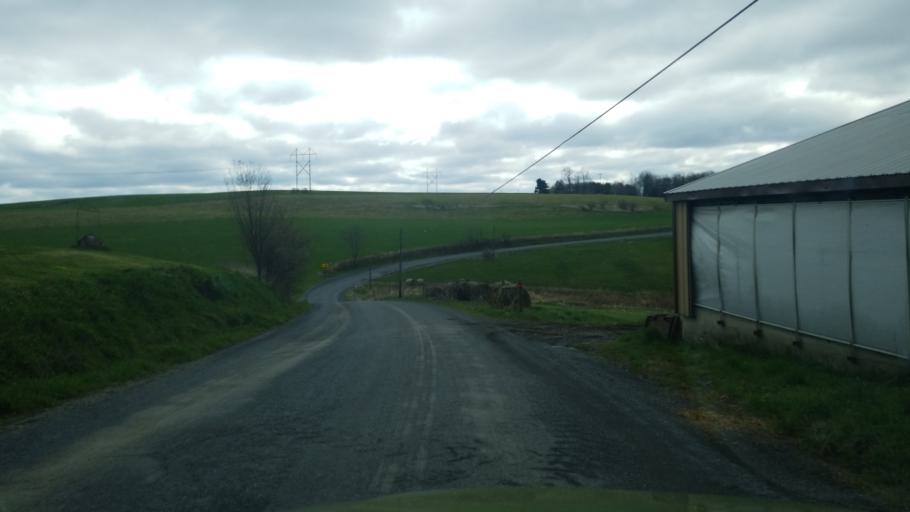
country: US
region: Pennsylvania
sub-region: Clearfield County
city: Clearfield
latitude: 41.0828
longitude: -78.3988
